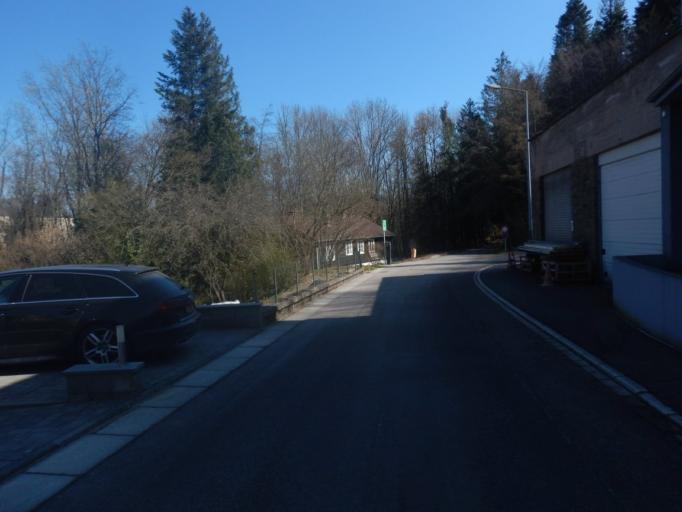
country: LU
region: Diekirch
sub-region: Canton de Wiltz
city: Wiltz
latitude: 49.9643
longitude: 5.9380
